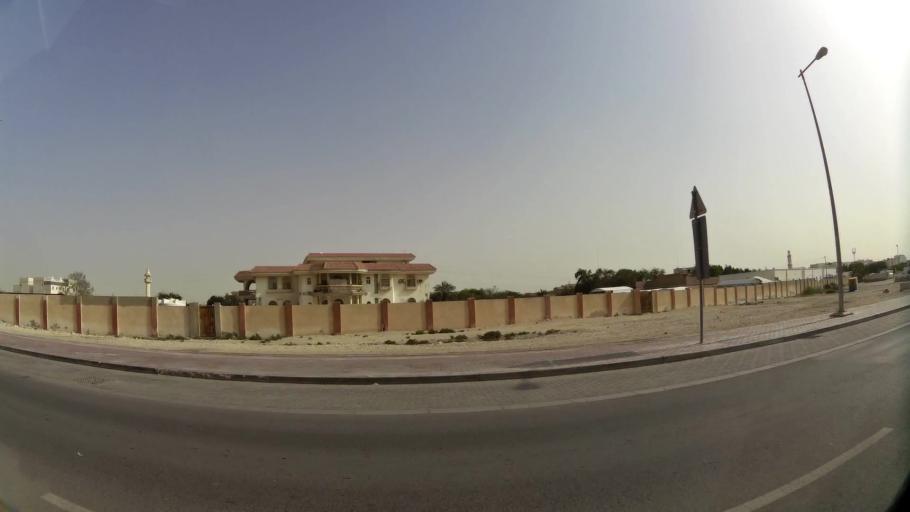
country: QA
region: Baladiyat ar Rayyan
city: Ar Rayyan
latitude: 25.2408
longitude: 51.4435
